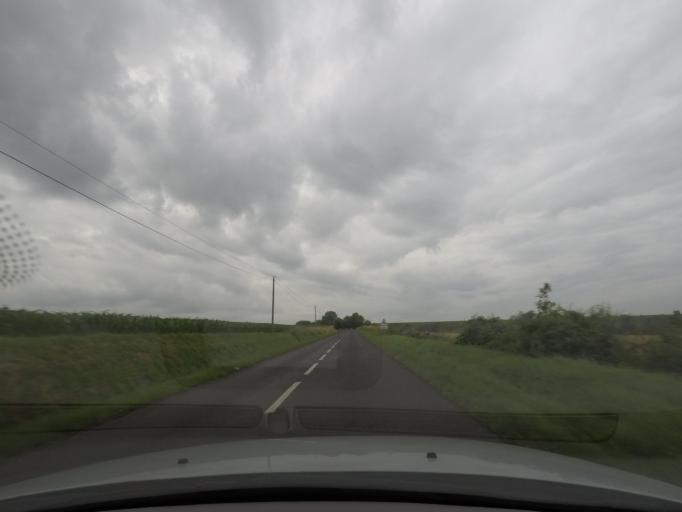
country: FR
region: Haute-Normandie
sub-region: Departement de la Seine-Maritime
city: Neufchatel-en-Bray
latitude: 49.7313
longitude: 1.4553
